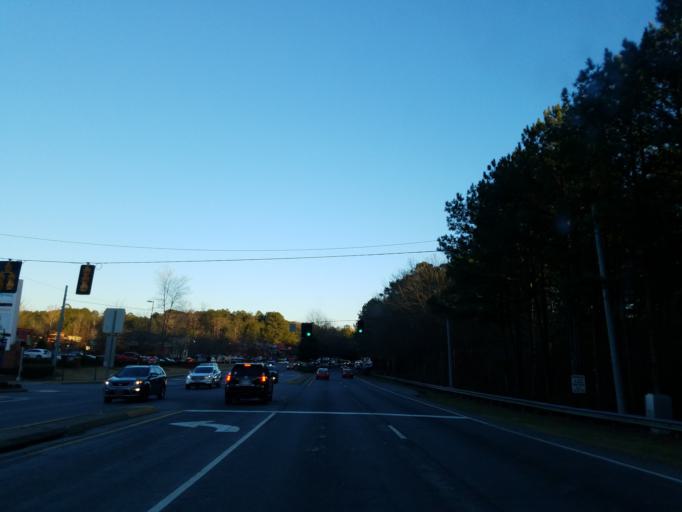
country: US
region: Georgia
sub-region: Cherokee County
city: Woodstock
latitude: 34.1048
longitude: -84.5423
